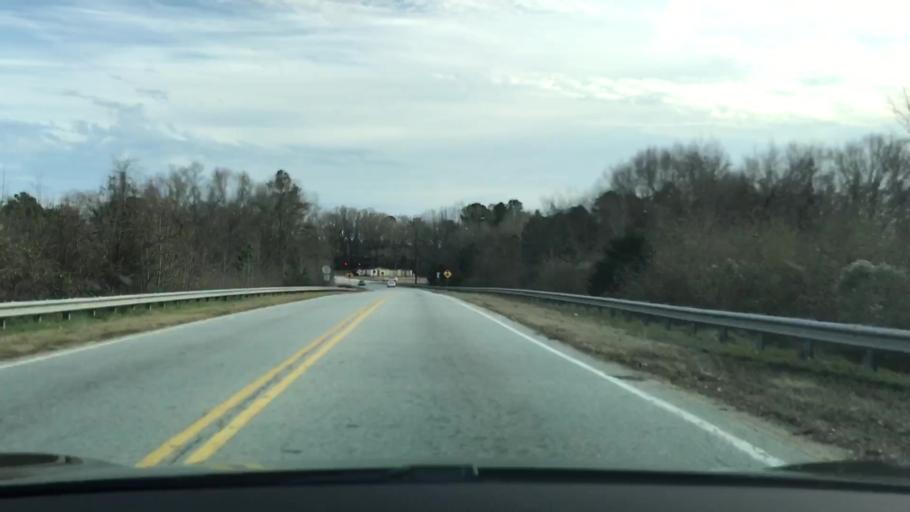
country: US
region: Georgia
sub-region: Warren County
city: West Warrenton
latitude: 33.4052
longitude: -82.6715
